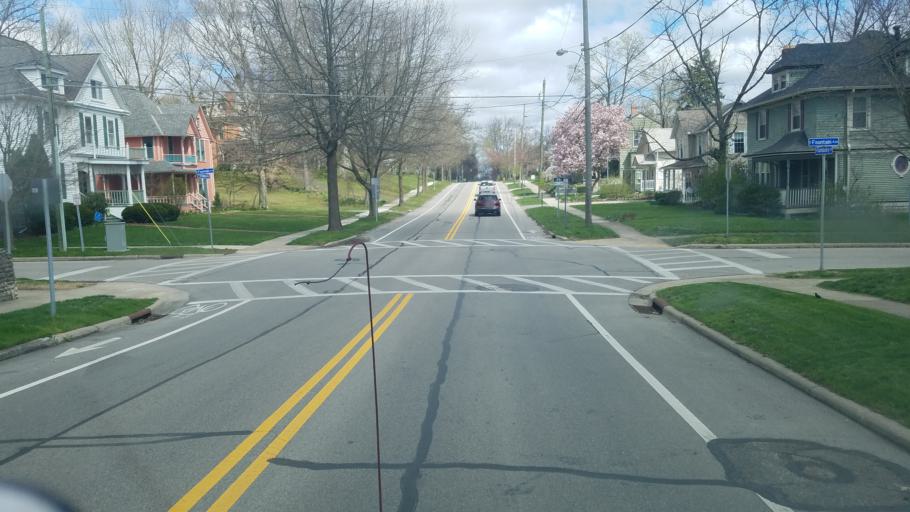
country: US
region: Ohio
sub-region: Delaware County
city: Delaware
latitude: 40.3080
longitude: -83.0671
